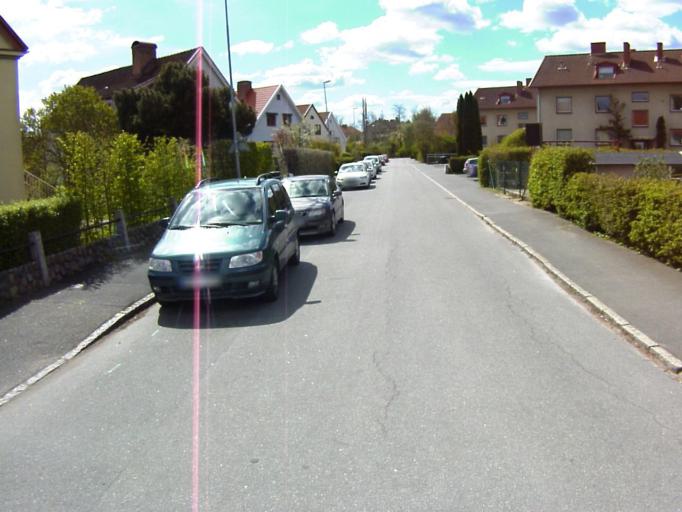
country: SE
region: Skane
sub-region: Kristianstads Kommun
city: Kristianstad
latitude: 56.0382
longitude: 14.1646
